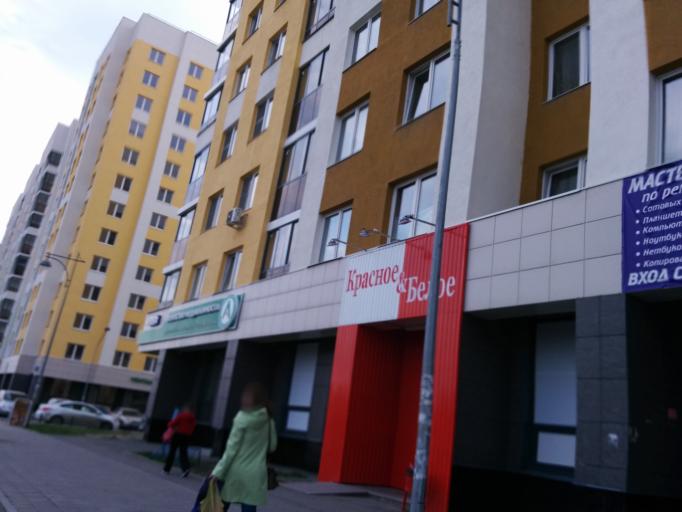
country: RU
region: Sverdlovsk
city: Sovkhoznyy
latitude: 56.7879
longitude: 60.5285
